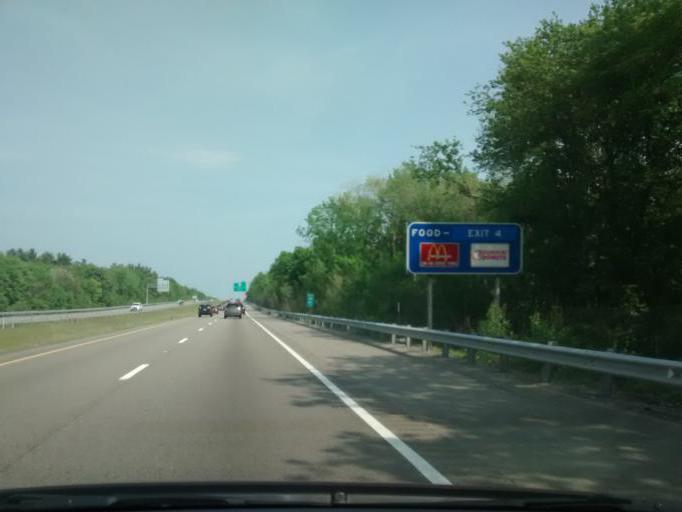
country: US
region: Massachusetts
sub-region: Plymouth County
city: Middleborough Center
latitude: 41.8891
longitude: -70.9375
